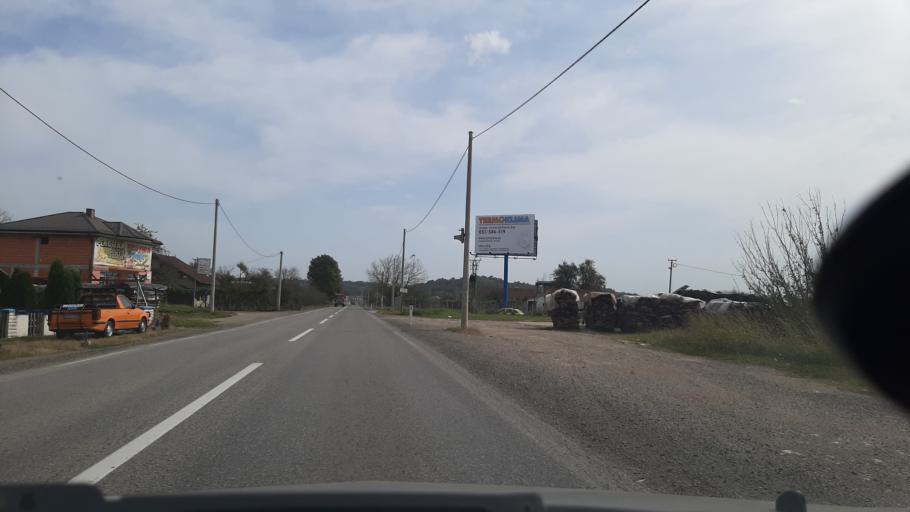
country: BA
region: Republika Srpska
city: Laktasi
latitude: 44.8774
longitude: 17.2986
